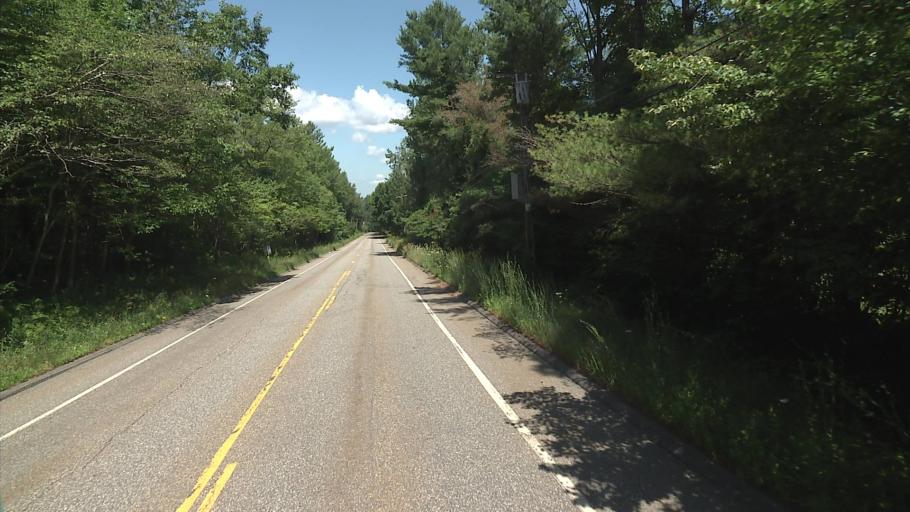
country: US
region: Connecticut
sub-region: Litchfield County
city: New Preston
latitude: 41.7844
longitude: -73.3577
